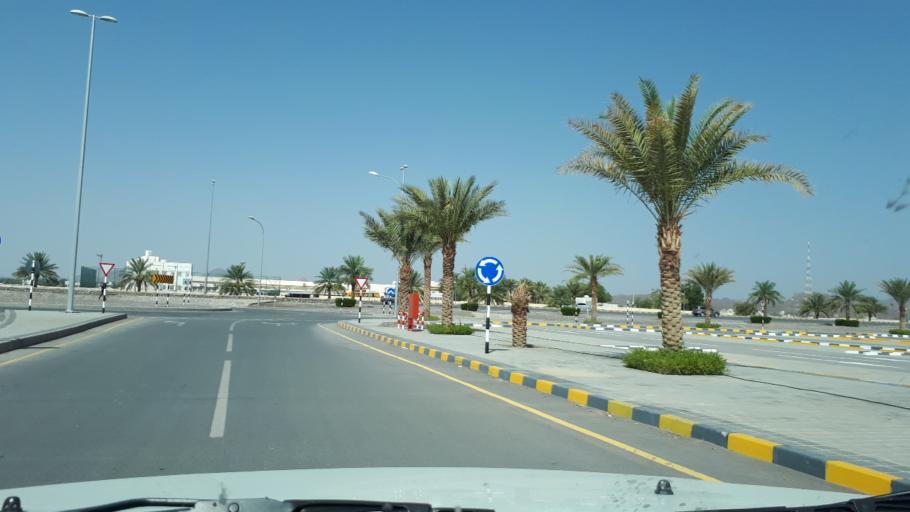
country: OM
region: Muhafazat ad Dakhiliyah
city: Nizwa
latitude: 22.8701
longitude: 57.5373
